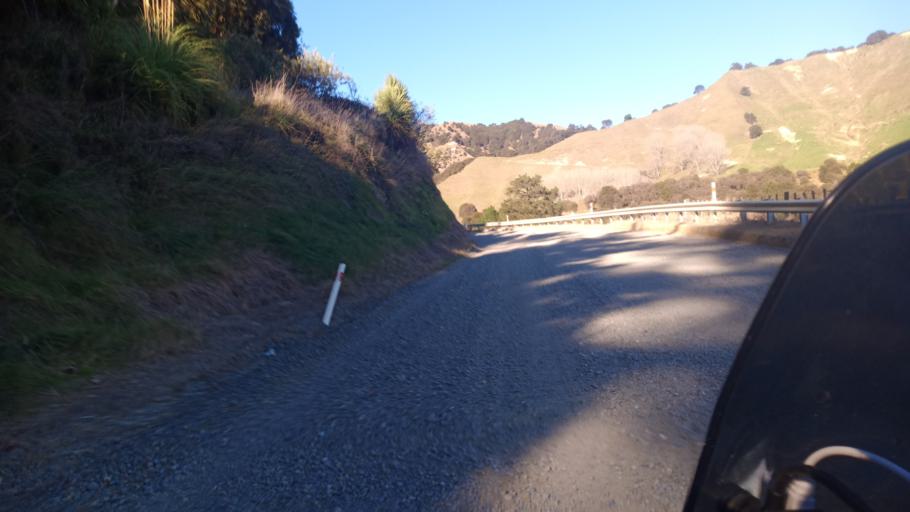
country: NZ
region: Hawke's Bay
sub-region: Wairoa District
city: Wairoa
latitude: -38.8673
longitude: 177.1991
